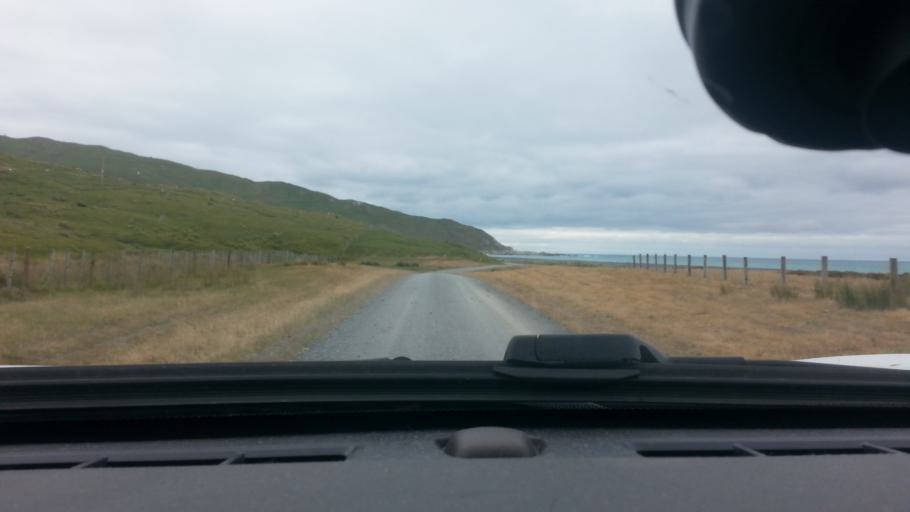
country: NZ
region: Wellington
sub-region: South Wairarapa District
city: Waipawa
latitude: -41.5643
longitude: 175.4066
